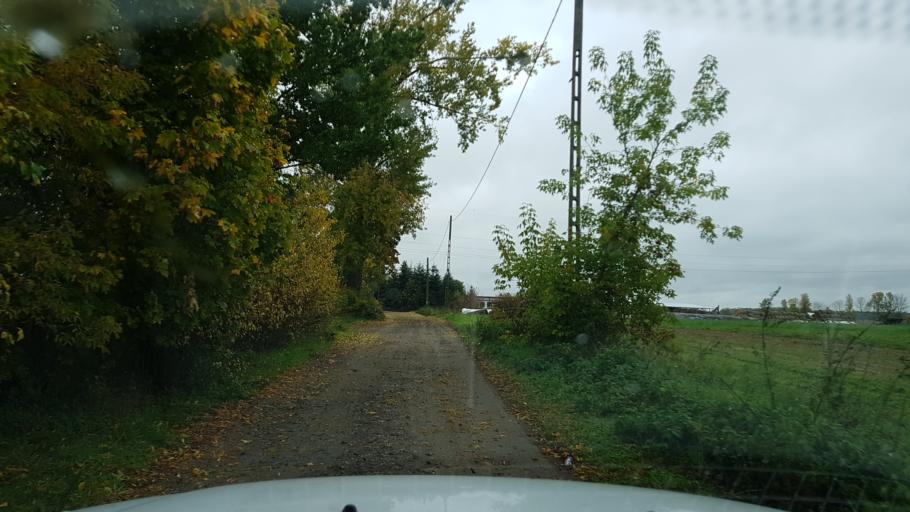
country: PL
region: West Pomeranian Voivodeship
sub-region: Powiat pyrzycki
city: Lipiany
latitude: 52.9704
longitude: 15.0110
